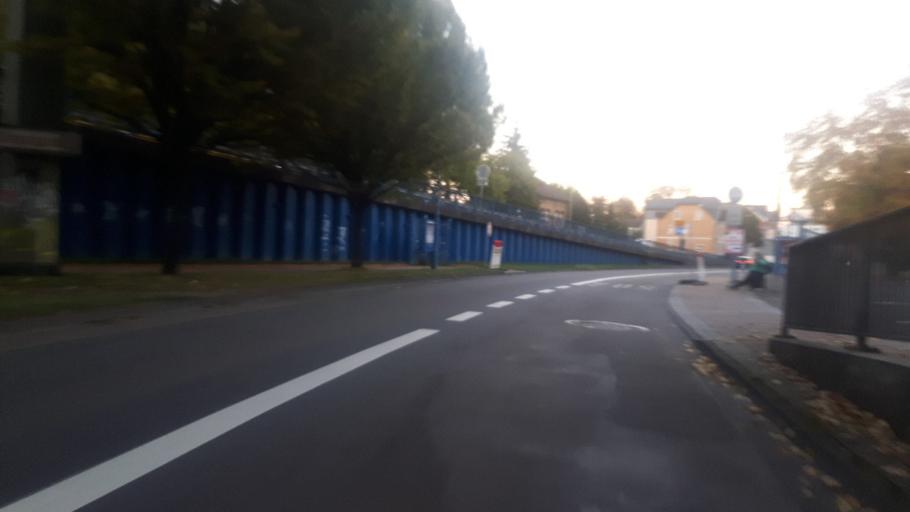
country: DE
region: North Rhine-Westphalia
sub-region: Regierungsbezirk Arnsberg
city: Siegen
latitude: 50.8677
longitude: 8.0087
